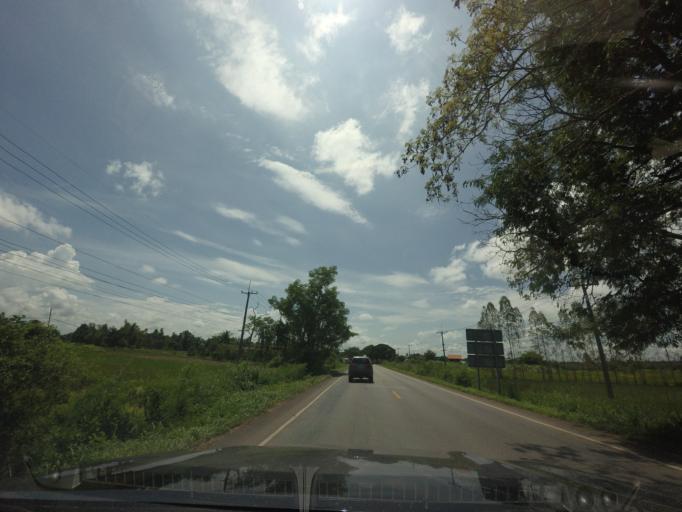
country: TH
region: Changwat Udon Thani
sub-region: Amphoe Ban Phue
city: Ban Phue
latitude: 17.7542
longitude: 102.3982
